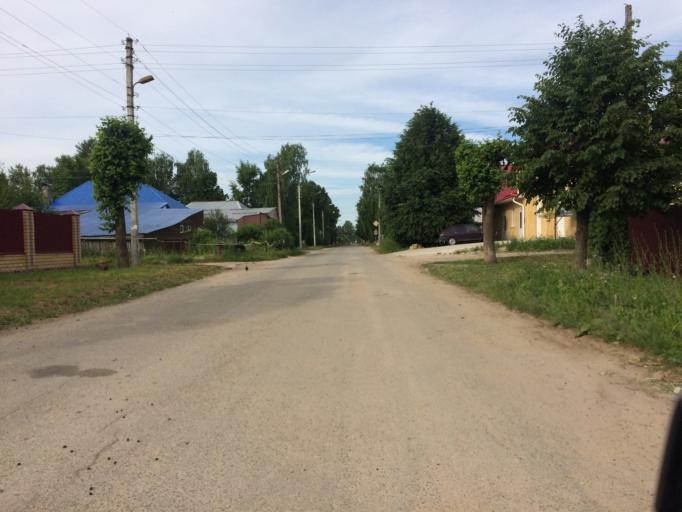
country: RU
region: Mariy-El
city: Yoshkar-Ola
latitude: 56.6525
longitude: 47.9164
